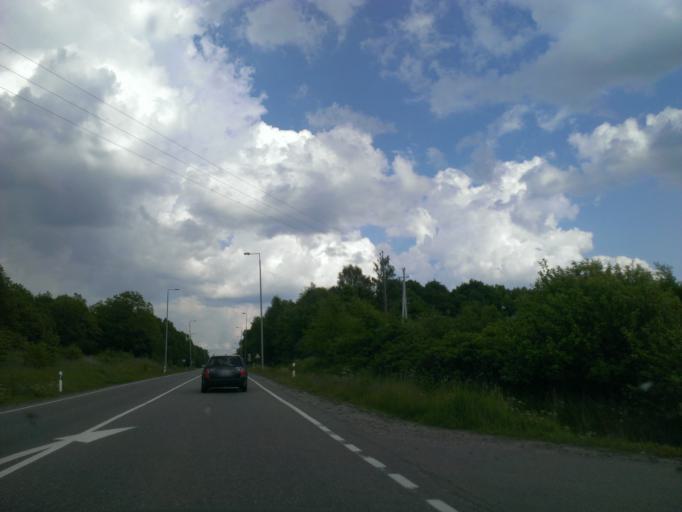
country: LT
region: Klaipedos apskritis
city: Kretinga
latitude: 55.8954
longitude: 21.1976
